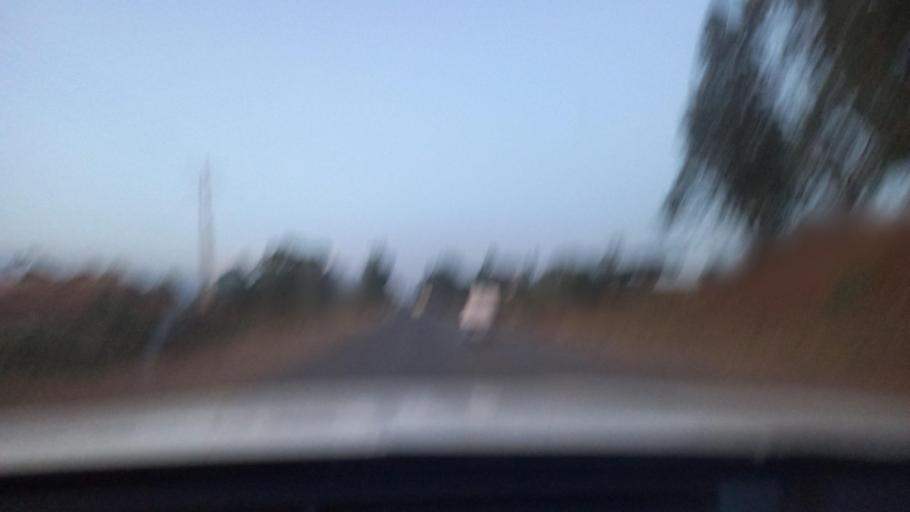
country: ET
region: Southern Nations, Nationalities, and People's Region
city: Butajira
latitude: 7.8607
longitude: 38.1918
